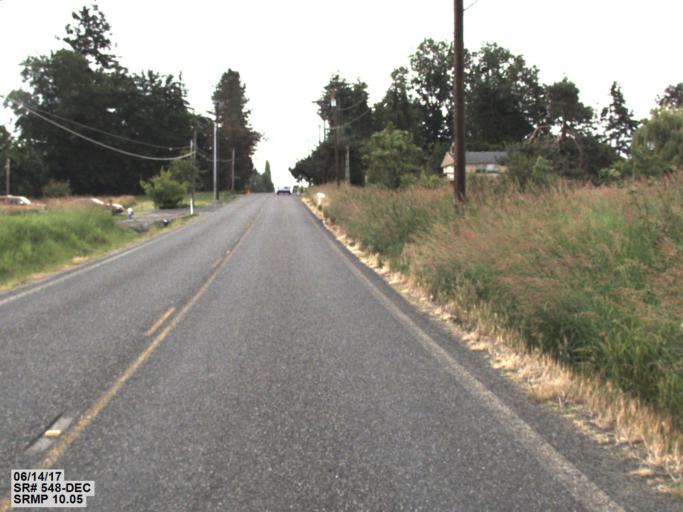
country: US
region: Washington
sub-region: Whatcom County
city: Birch Bay
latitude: 48.9516
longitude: -122.7261
